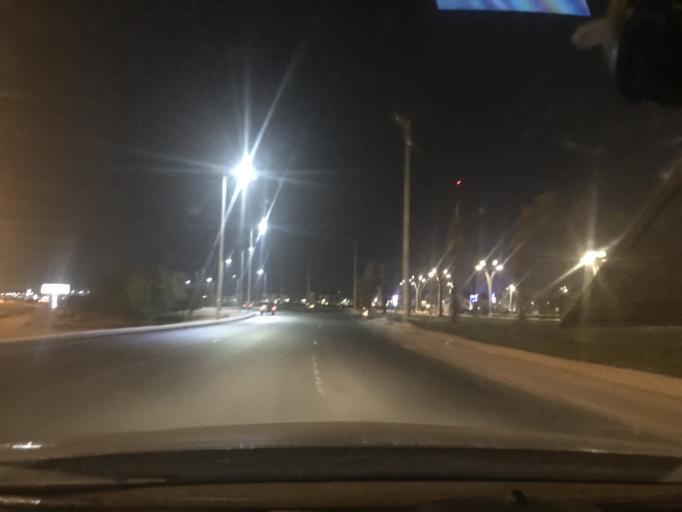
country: SA
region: Ar Riyad
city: Riyadh
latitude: 24.8375
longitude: 46.7282
